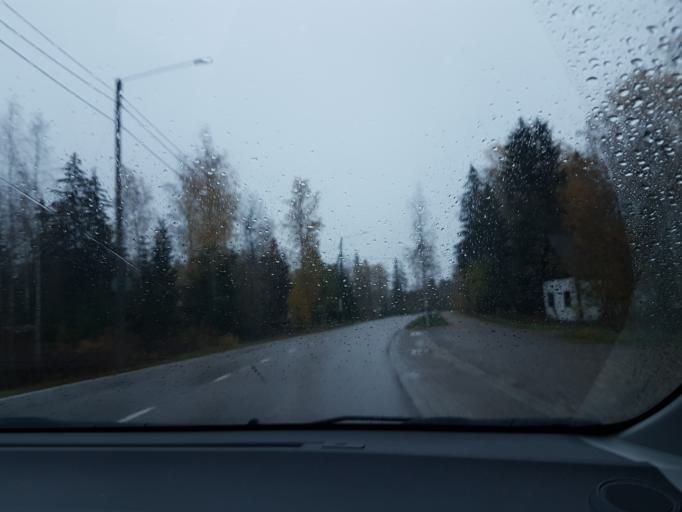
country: FI
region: Uusimaa
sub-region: Helsinki
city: Jaervenpaeae
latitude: 60.5659
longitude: 25.1384
